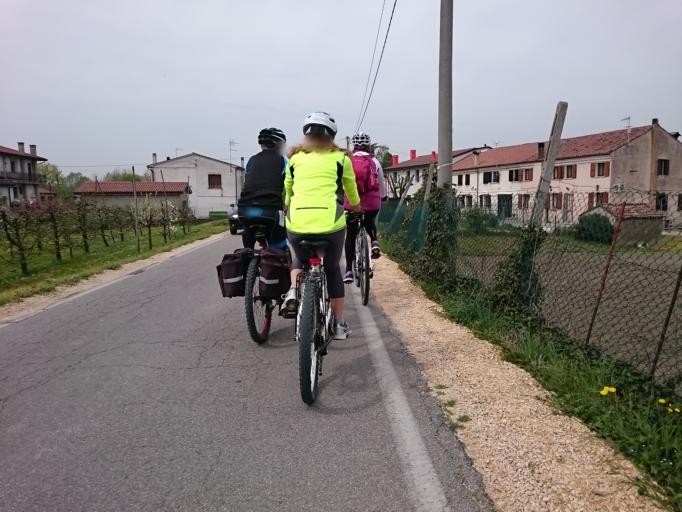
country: IT
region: Veneto
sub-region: Provincia di Padova
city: Anguillara Veneta
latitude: 45.1478
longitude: 11.8701
